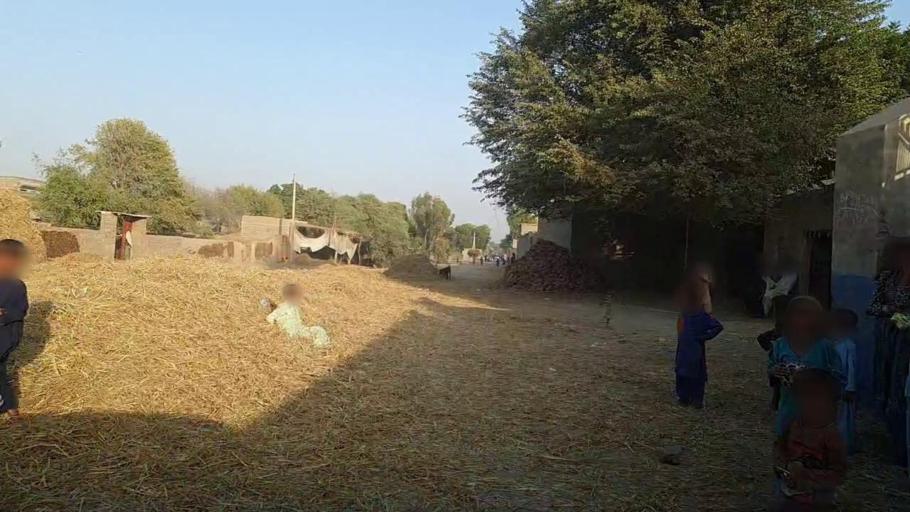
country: PK
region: Sindh
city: Kashmor
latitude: 28.4279
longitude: 69.4703
